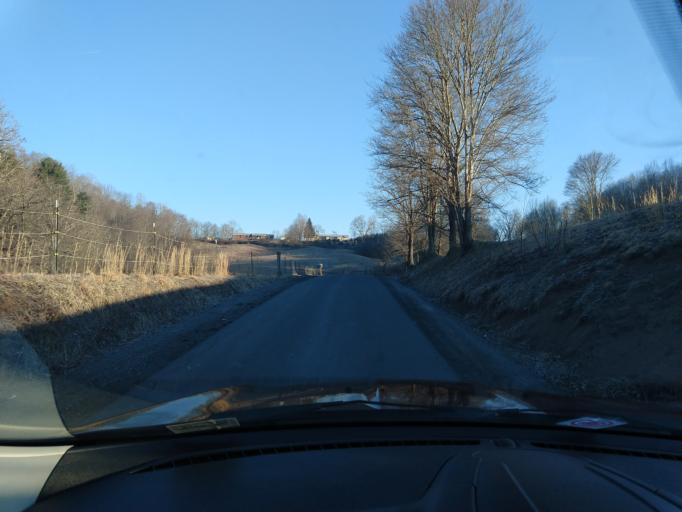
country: US
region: West Virginia
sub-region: Greenbrier County
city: Rainelle
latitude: 37.8694
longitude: -80.7273
